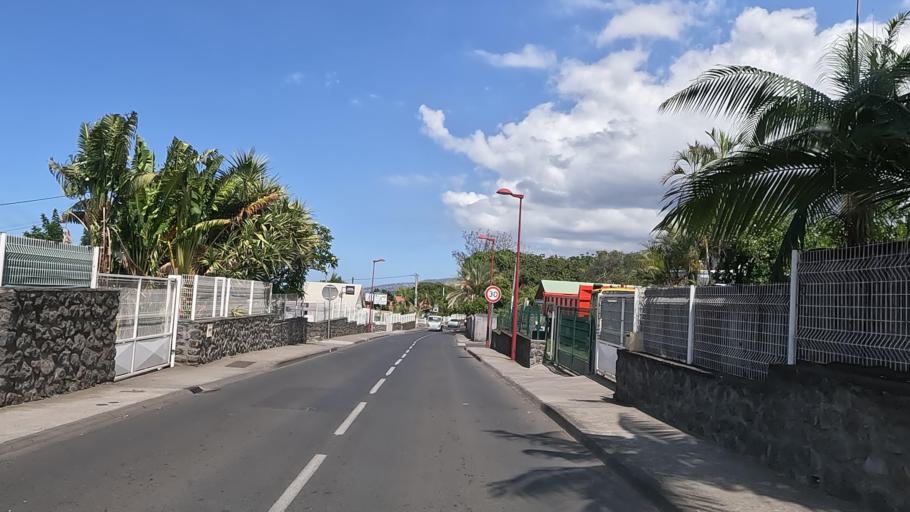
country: RE
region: Reunion
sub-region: Reunion
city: Saint-Louis
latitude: -21.2767
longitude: 55.4442
